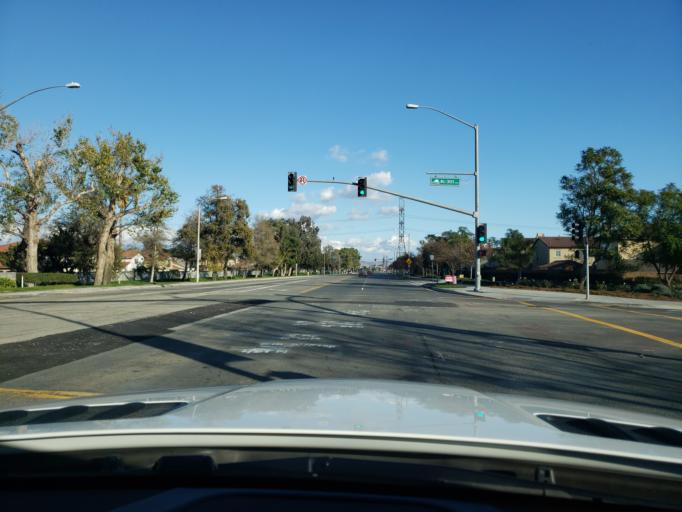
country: US
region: California
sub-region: Riverside County
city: Mira Loma
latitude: 34.0189
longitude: -117.5674
